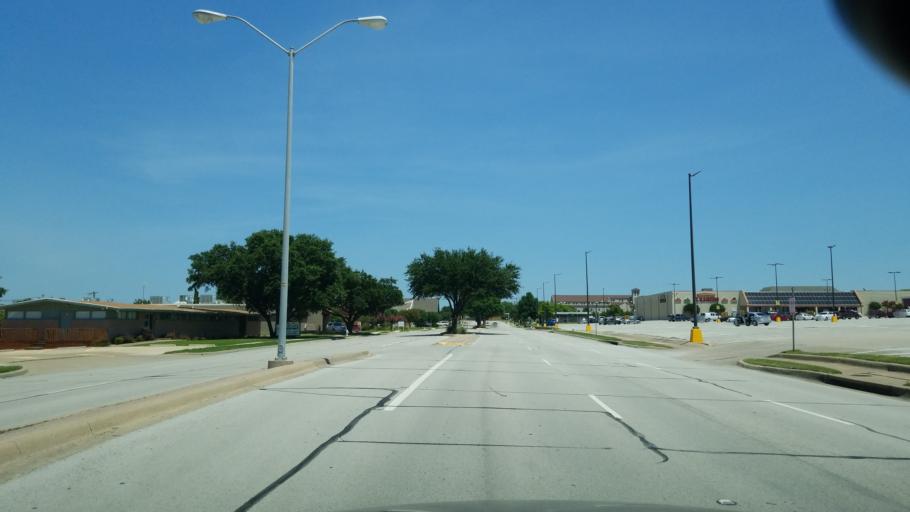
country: US
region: Texas
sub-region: Dallas County
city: Farmers Branch
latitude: 32.9382
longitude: -96.8893
